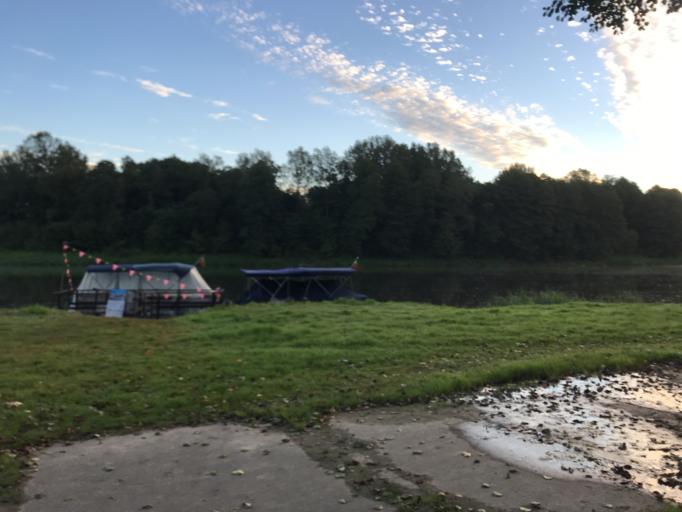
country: LT
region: Alytaus apskritis
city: Druskininkai
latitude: 54.0190
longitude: 23.9808
